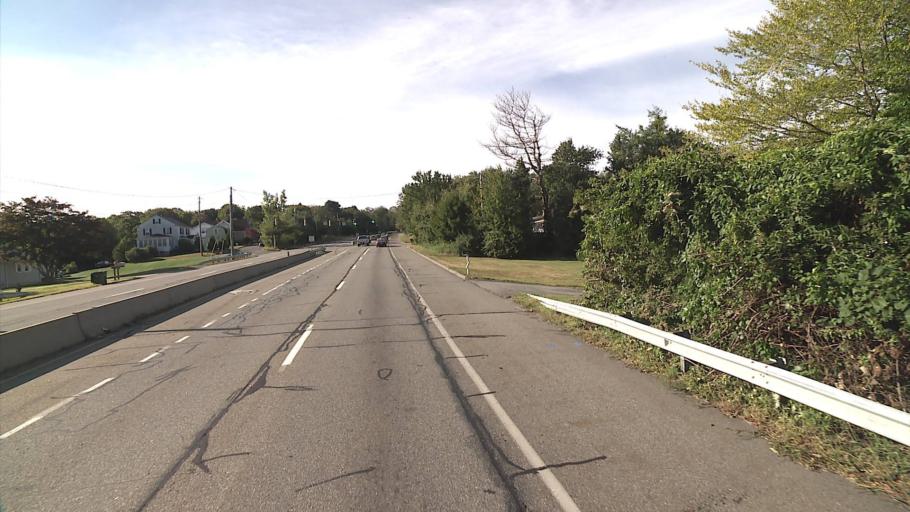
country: US
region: Connecticut
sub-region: New London County
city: Conning Towers-Nautilus Park
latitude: 41.3946
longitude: -72.1056
